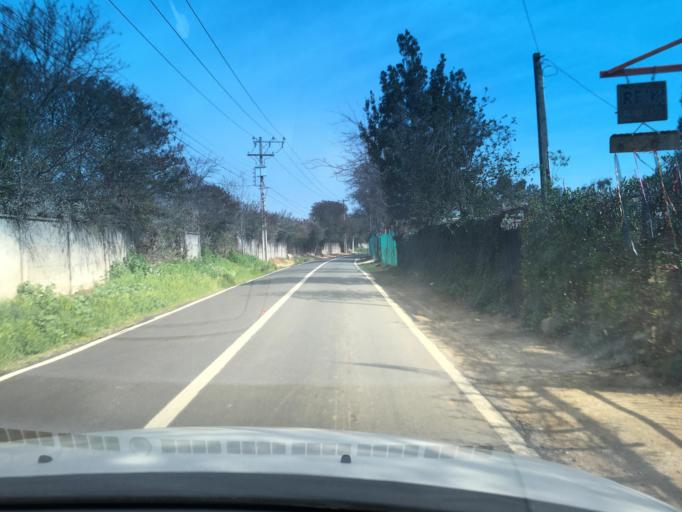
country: CL
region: Valparaiso
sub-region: Provincia de Marga Marga
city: Limache
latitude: -33.0125
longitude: -71.2084
